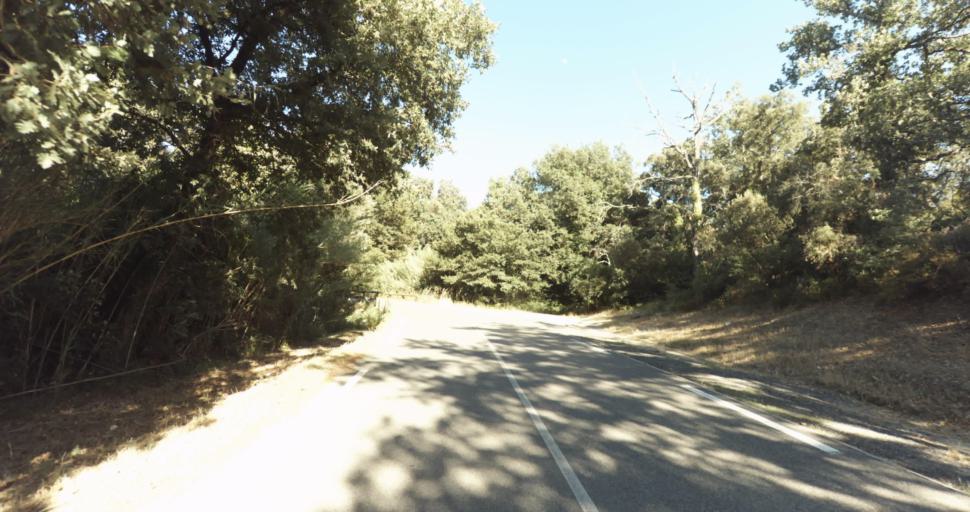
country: FR
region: Provence-Alpes-Cote d'Azur
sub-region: Departement du Var
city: Gassin
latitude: 43.2520
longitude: 6.5978
